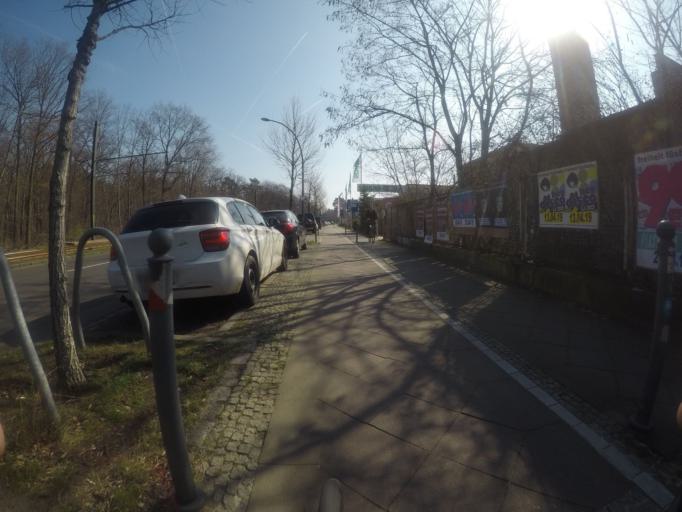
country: DE
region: Berlin
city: Friedrichshagen
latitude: 52.4493
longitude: 13.6081
